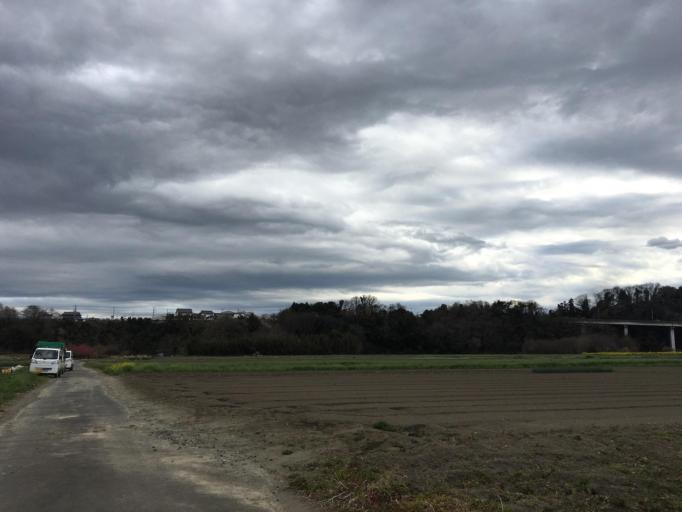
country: JP
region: Saitama
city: Yorii
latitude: 36.1167
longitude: 139.2491
